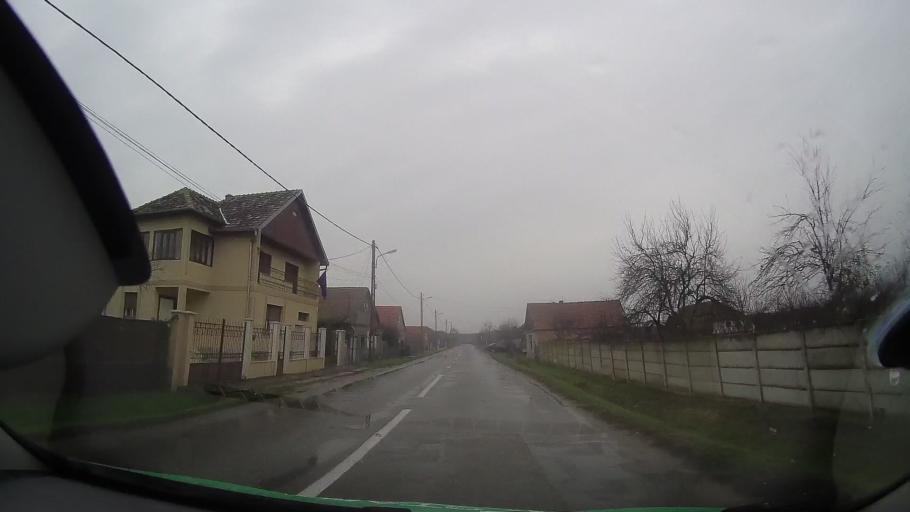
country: RO
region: Bihor
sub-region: Comuna Tinca
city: Gurbediu
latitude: 46.7903
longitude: 21.8548
